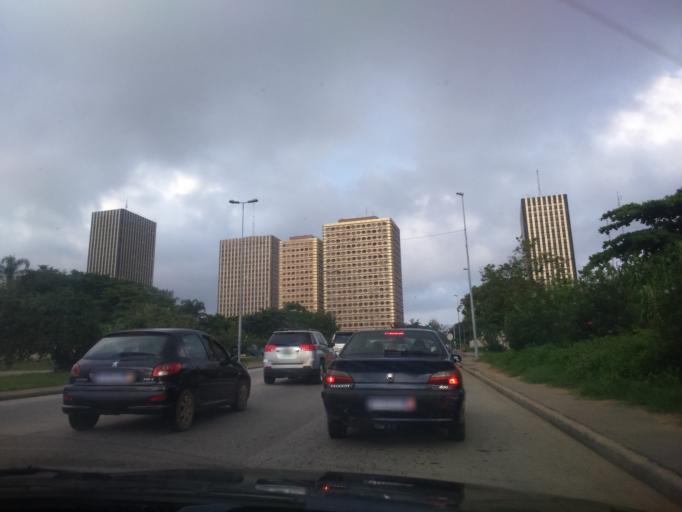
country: CI
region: Lagunes
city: Abidjan
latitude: 5.3348
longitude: -4.0202
